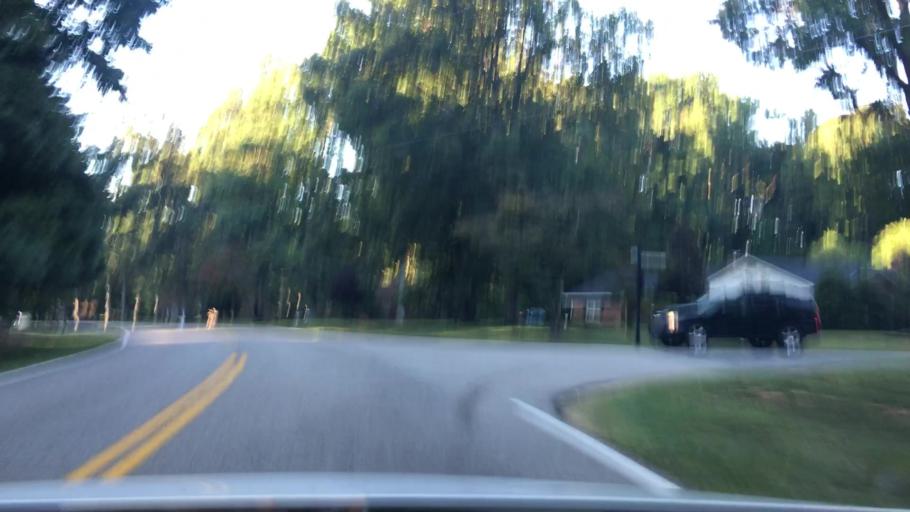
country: US
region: Virginia
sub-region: Chesterfield County
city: Bon Air
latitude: 37.5310
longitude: -77.6413
